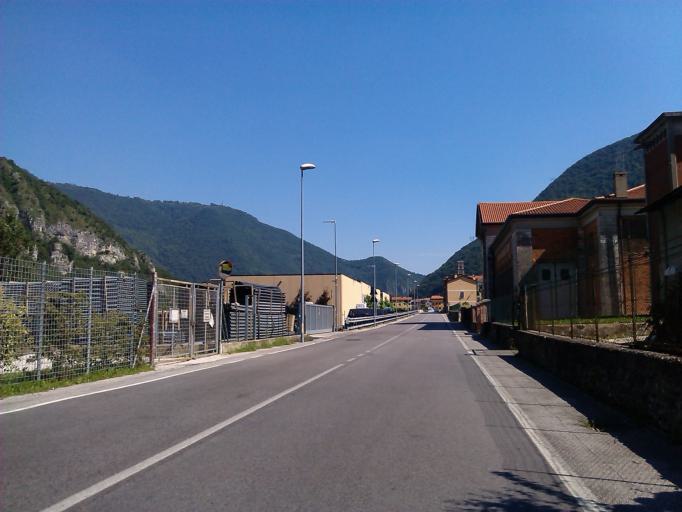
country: IT
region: Veneto
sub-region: Provincia di Vicenza
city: Campolongo sul Brenta
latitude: 45.8319
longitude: 11.6969
